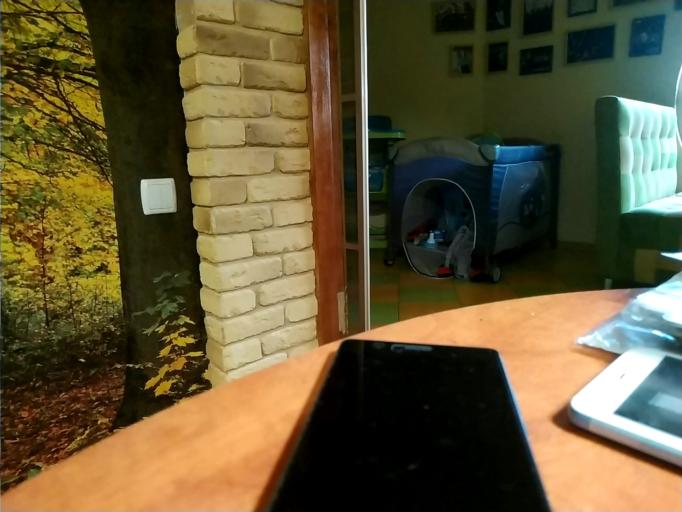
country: RU
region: Orjol
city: Znamenskoye
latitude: 53.6044
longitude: 35.4677
